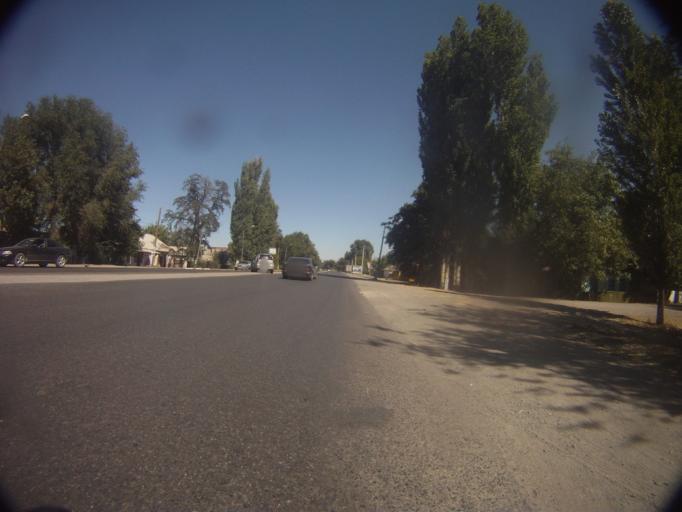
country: KG
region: Chuy
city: Sokuluk
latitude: 42.8657
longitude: 74.3518
